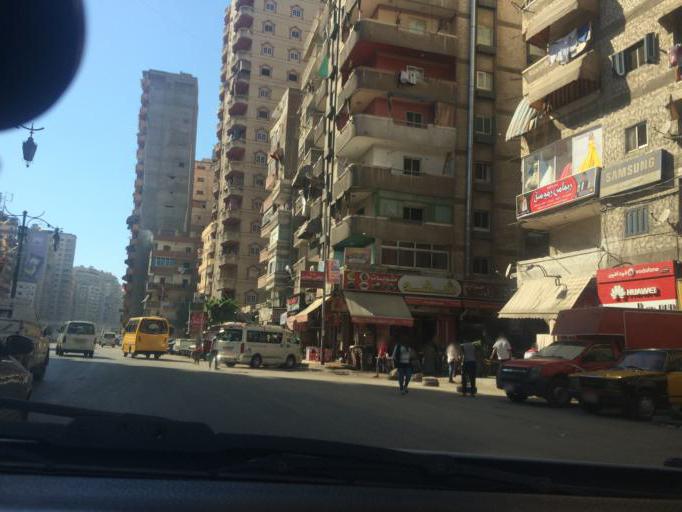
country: EG
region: Alexandria
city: Alexandria
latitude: 31.2649
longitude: 30.0045
